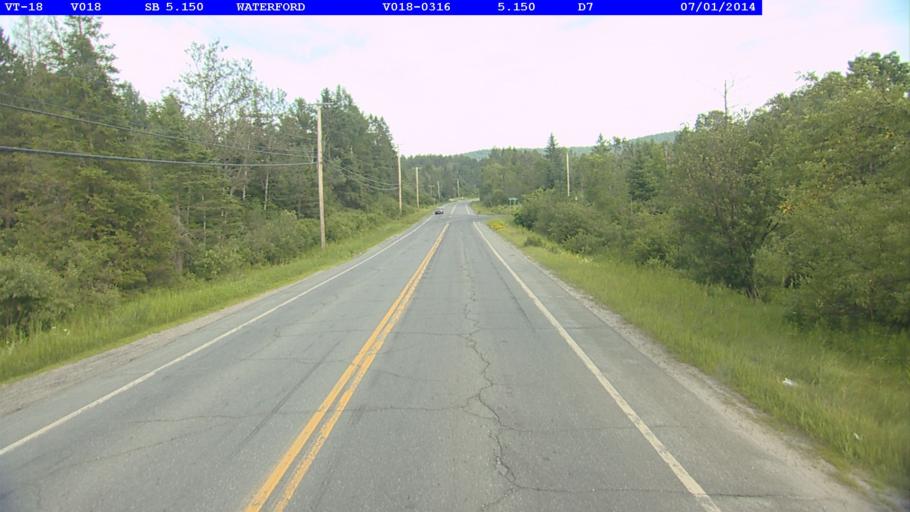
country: US
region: Vermont
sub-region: Caledonia County
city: Saint Johnsbury
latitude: 44.4051
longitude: -71.9257
